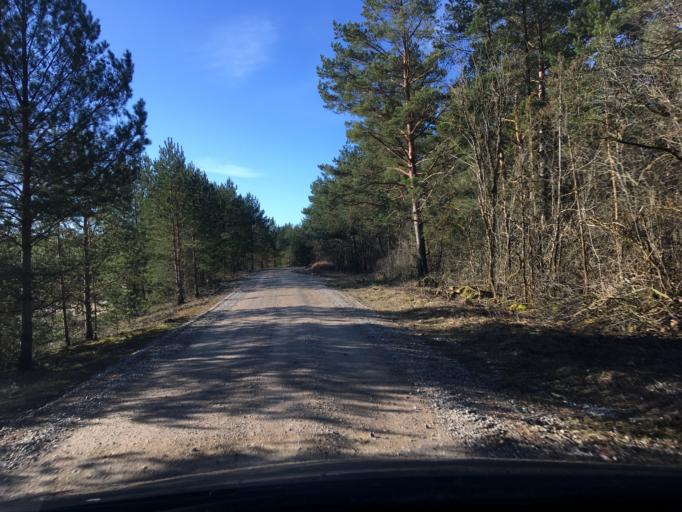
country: EE
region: Laeaene
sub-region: Lihula vald
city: Lihula
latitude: 58.5790
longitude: 23.7026
